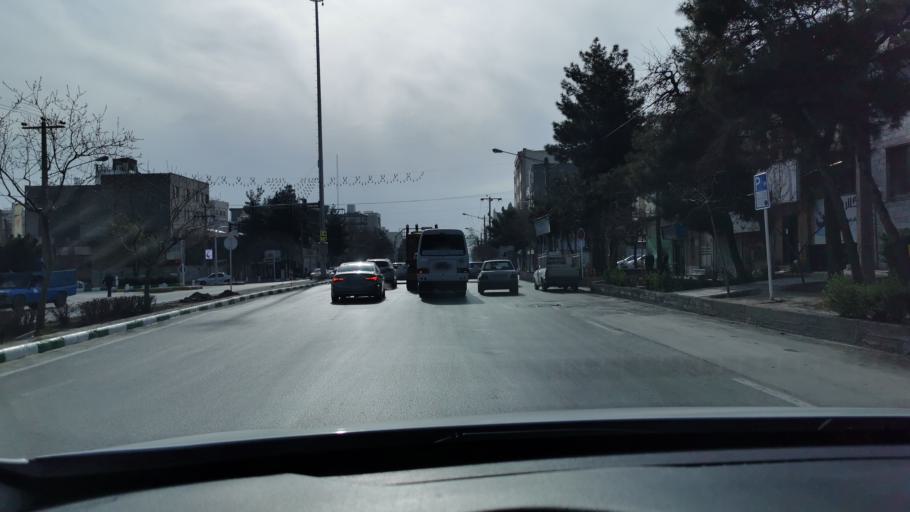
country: IR
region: Razavi Khorasan
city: Mashhad
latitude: 36.2913
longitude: 59.5371
